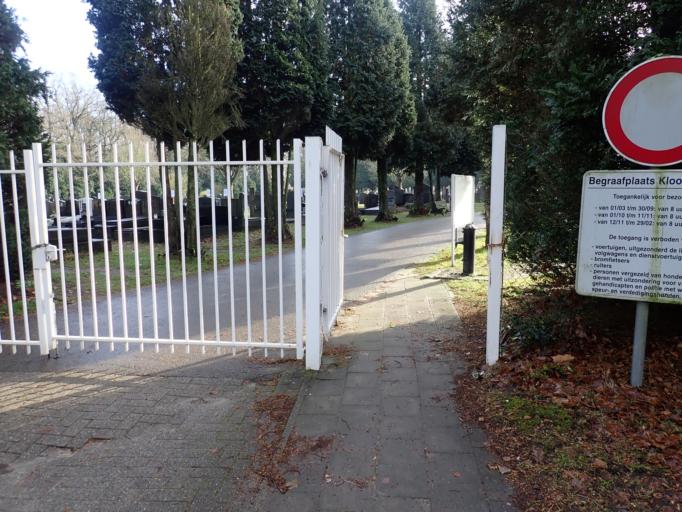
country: BE
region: Flanders
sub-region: Provincie Antwerpen
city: Lier
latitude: 51.1432
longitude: 4.5936
